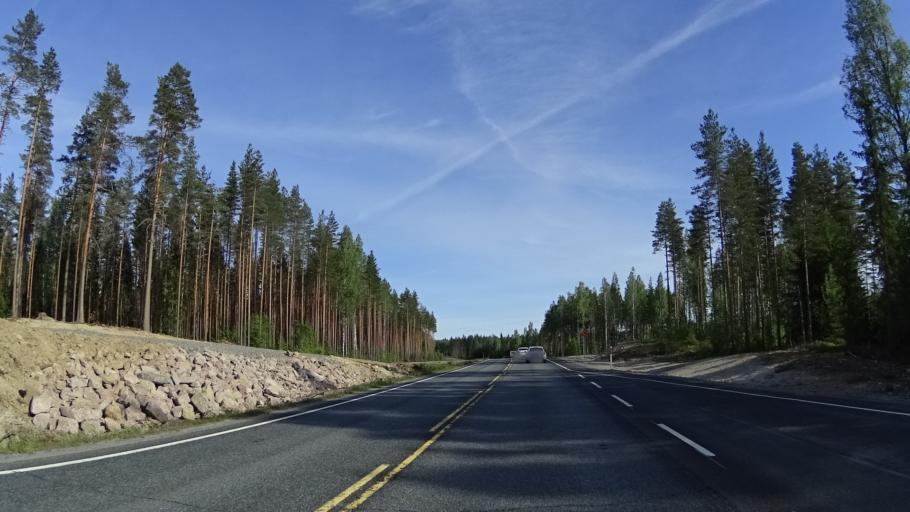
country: FI
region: Haeme
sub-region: Forssa
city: Tammela
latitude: 60.7196
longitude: 23.7529
